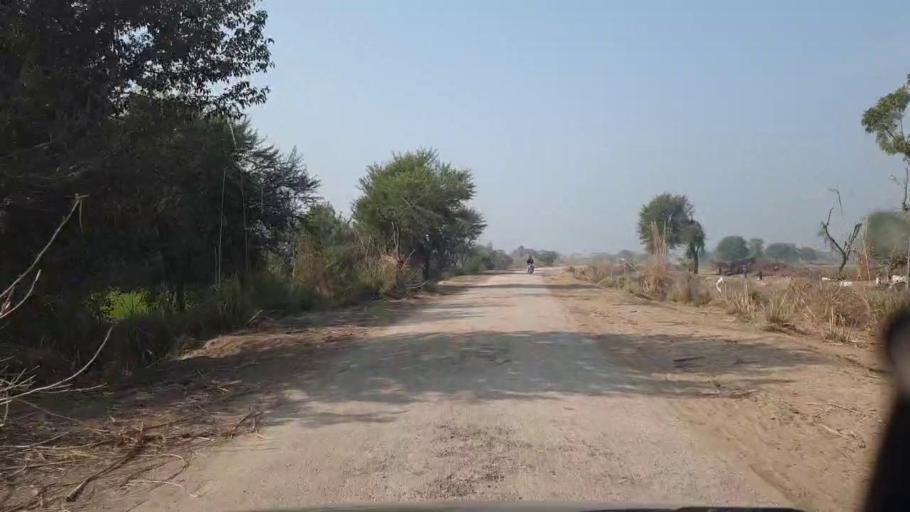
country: PK
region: Sindh
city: Shahdadpur
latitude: 26.0340
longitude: 68.5374
